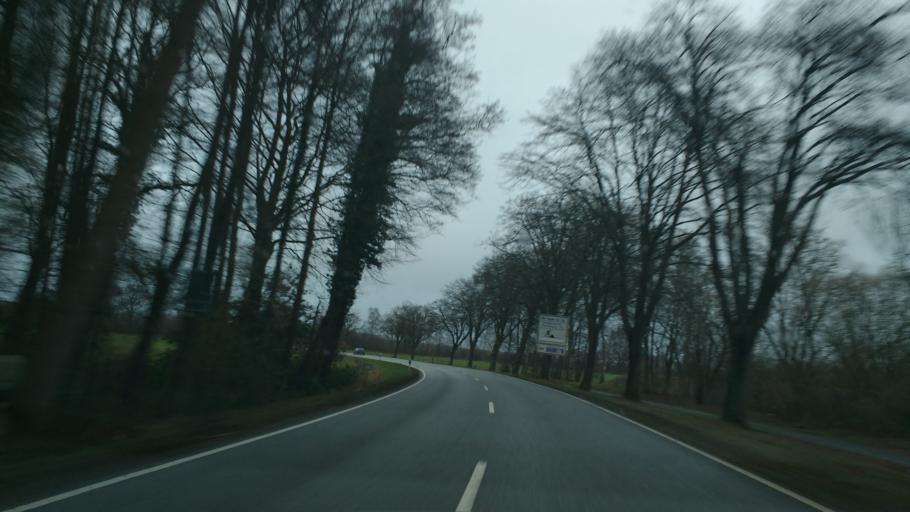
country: DE
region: Schleswig-Holstein
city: Jahrsdorf
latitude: 54.0731
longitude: 9.6498
